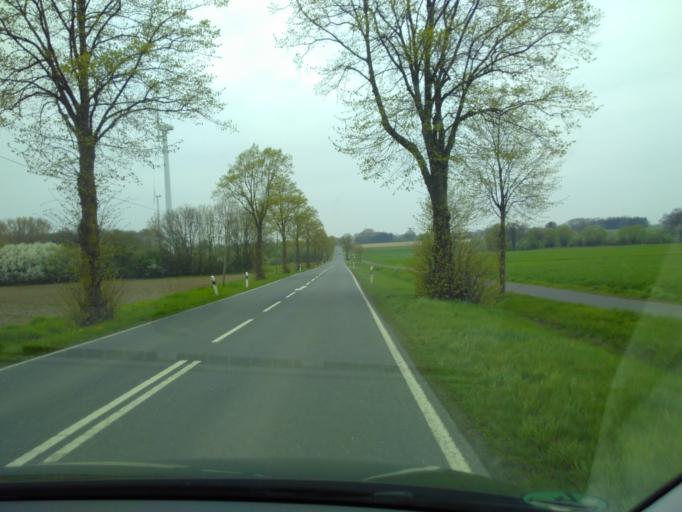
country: DE
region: North Rhine-Westphalia
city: Oelde
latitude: 51.7742
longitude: 8.1496
